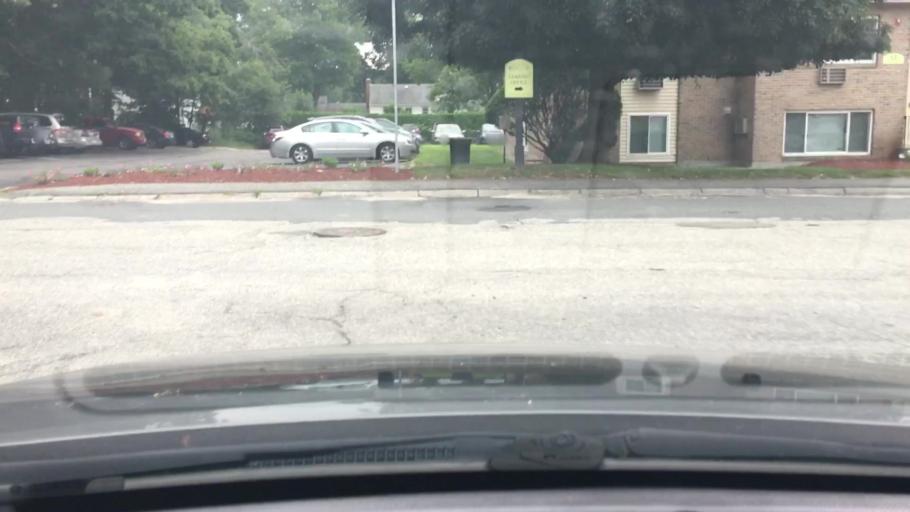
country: US
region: Massachusetts
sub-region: Worcester County
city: Hopedale
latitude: 42.1567
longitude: -71.5369
